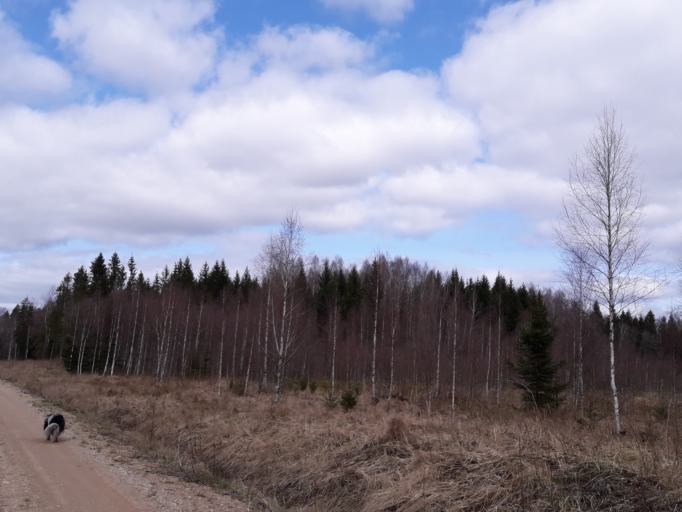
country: LV
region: Talsu Rajons
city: Sabile
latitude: 56.8953
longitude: 22.3793
